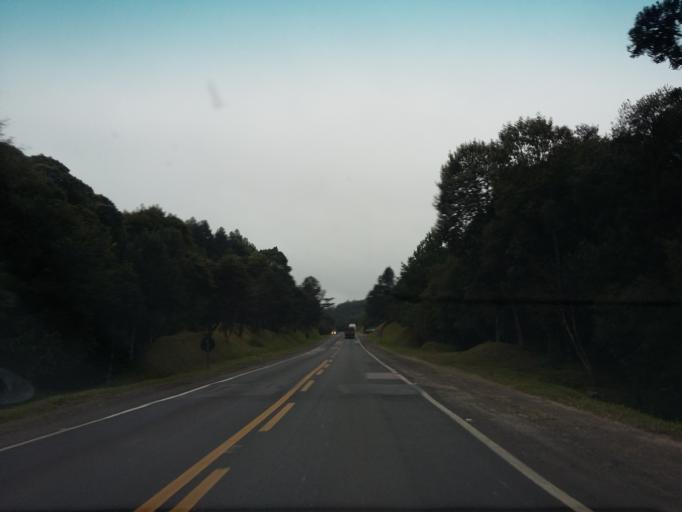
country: BR
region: Santa Catarina
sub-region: Santa Cecilia
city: Santa Cecilia
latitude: -26.6178
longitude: -50.2357
